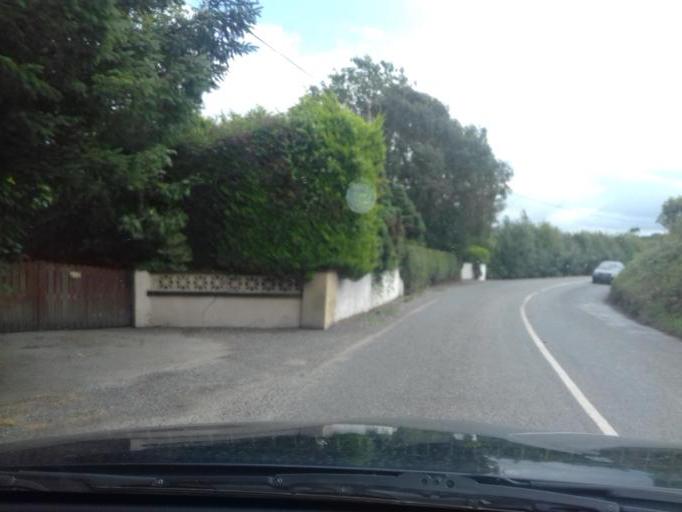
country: IE
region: Leinster
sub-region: Loch Garman
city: Enniscorthy
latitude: 52.4982
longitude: -6.5170
